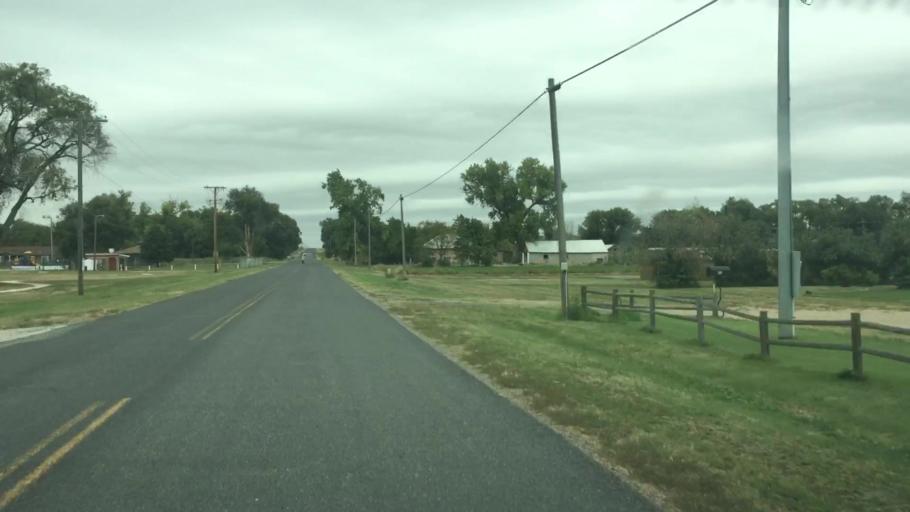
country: US
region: Kansas
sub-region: Hamilton County
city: Syracuse
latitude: 38.0553
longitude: -102.1186
